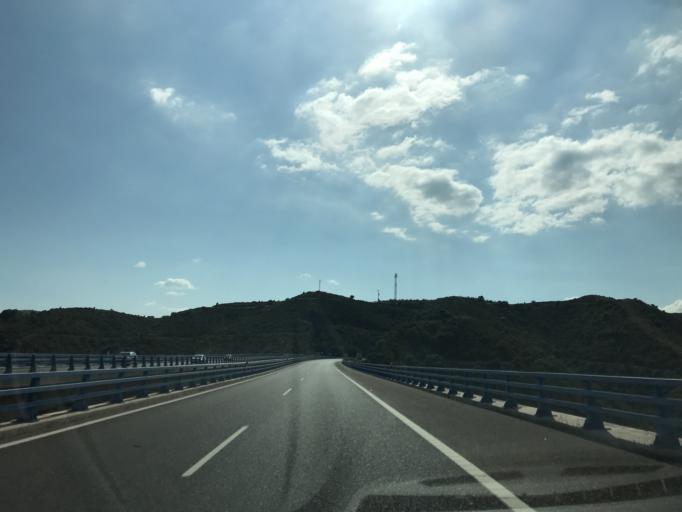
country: ES
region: Andalusia
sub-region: Provincia de Malaga
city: Istan
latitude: 36.5264
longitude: -4.9548
